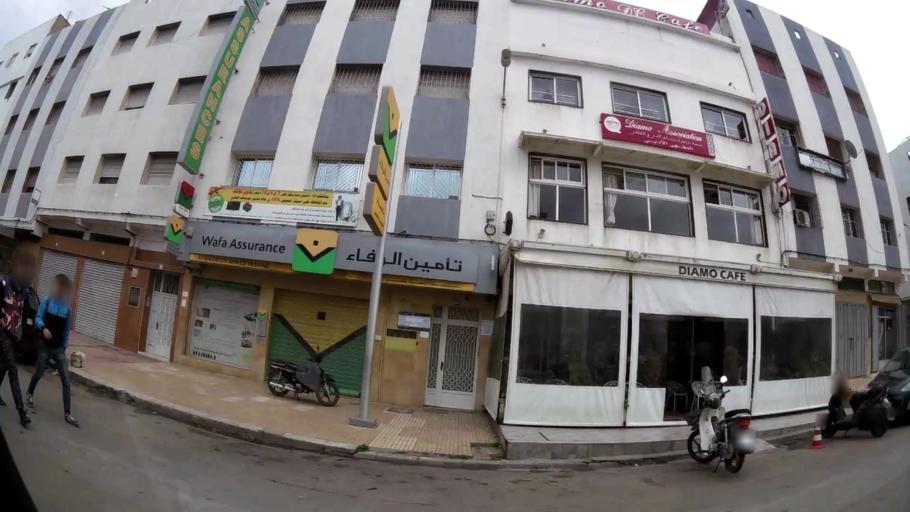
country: MA
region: Grand Casablanca
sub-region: Mediouna
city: Tit Mellil
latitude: 33.6105
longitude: -7.5123
